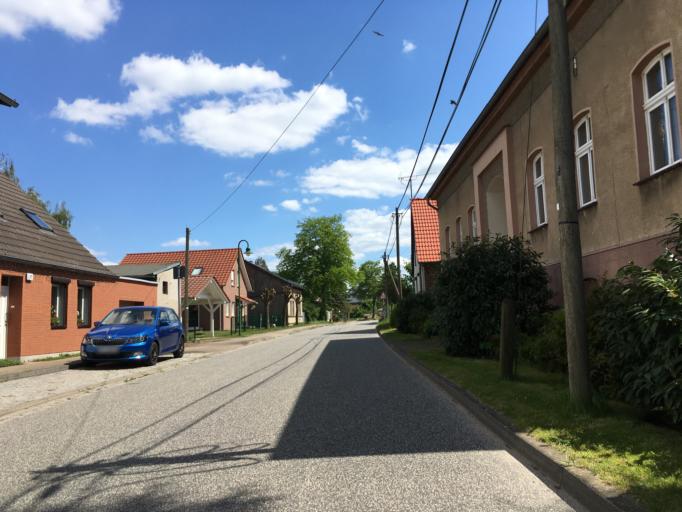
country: DE
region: Brandenburg
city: Biesenthal
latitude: 52.7349
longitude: 13.6646
